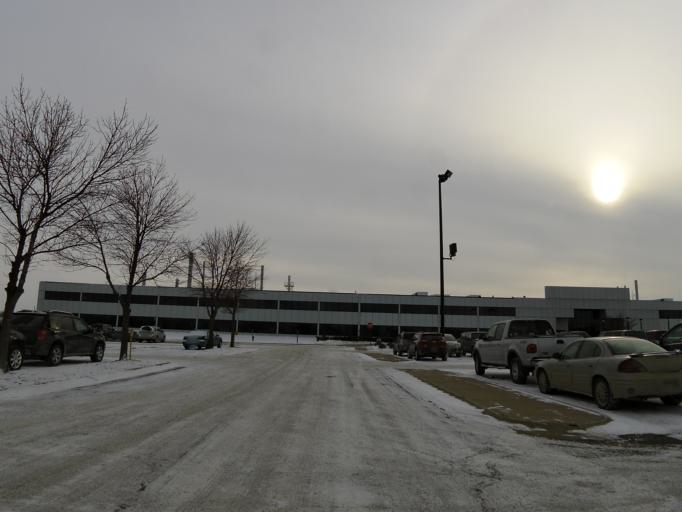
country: US
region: Minnesota
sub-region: McLeod County
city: Hutchinson
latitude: 44.9003
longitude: -94.3535
